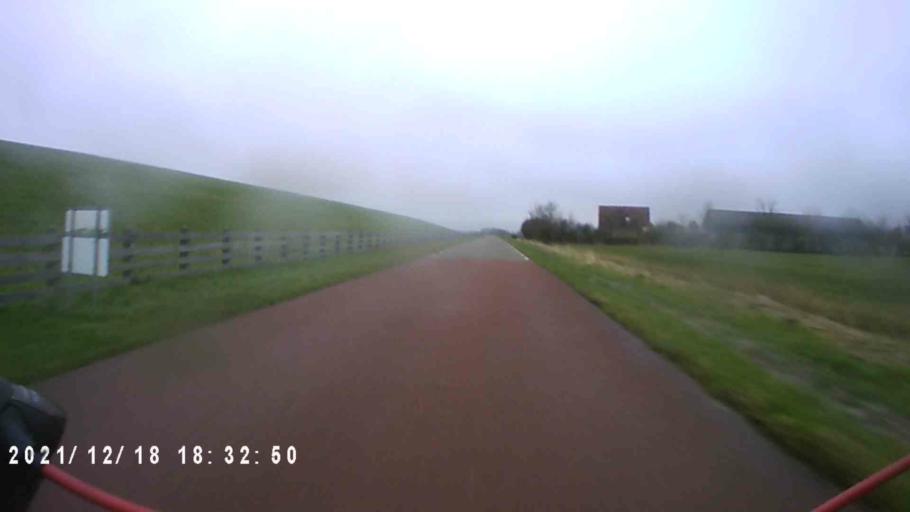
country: NL
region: Friesland
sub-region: Gemeente Dongeradeel
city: Ternaard
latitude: 53.4023
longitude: 6.0197
